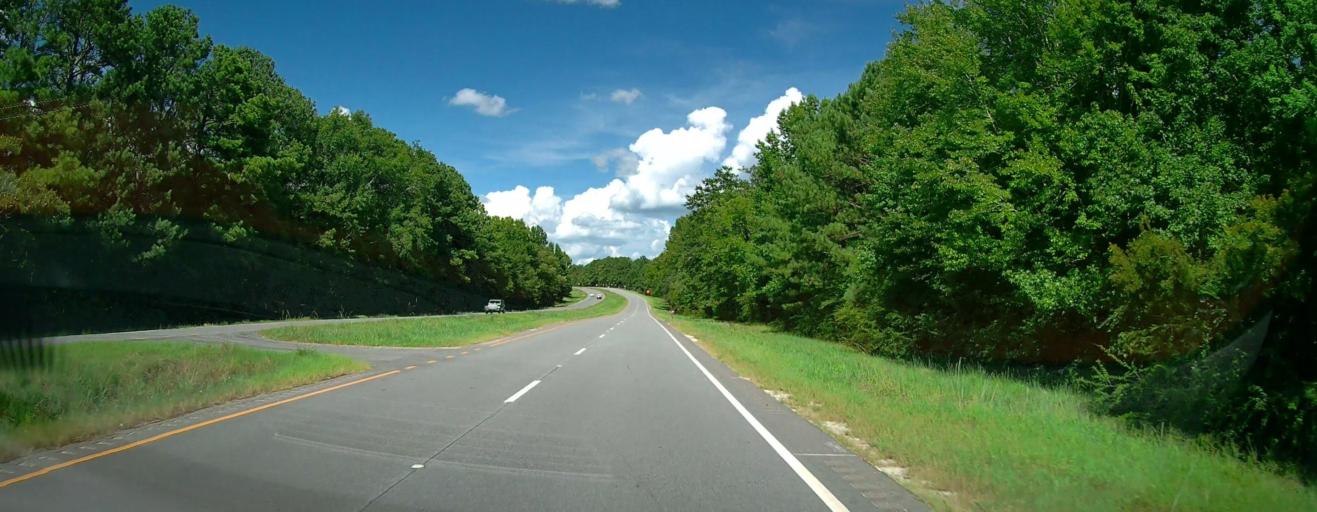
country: US
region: Alabama
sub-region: Macon County
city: Tuskegee
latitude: 32.3838
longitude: -85.7648
